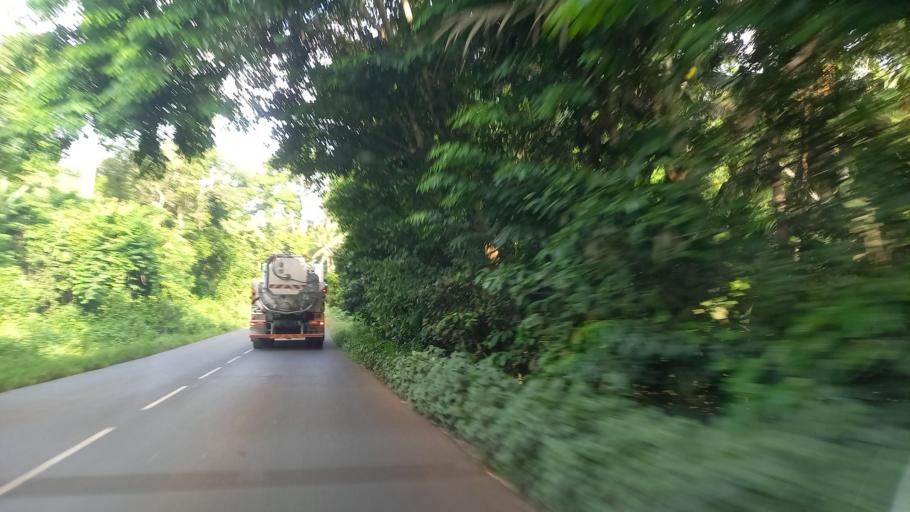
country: YT
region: Chiconi
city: Chiconi
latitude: -12.8164
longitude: 45.1298
